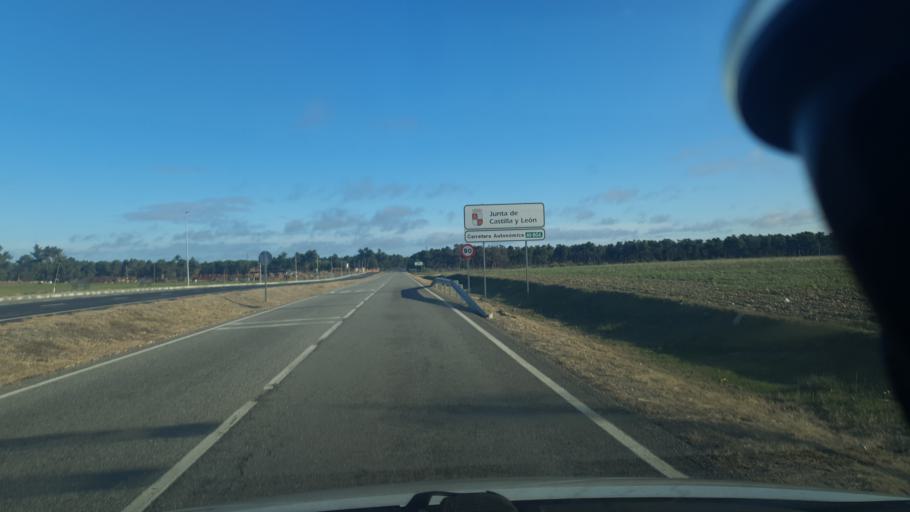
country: ES
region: Castille and Leon
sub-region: Provincia de Avila
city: Tinosillos
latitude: 40.9399
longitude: -4.7238
